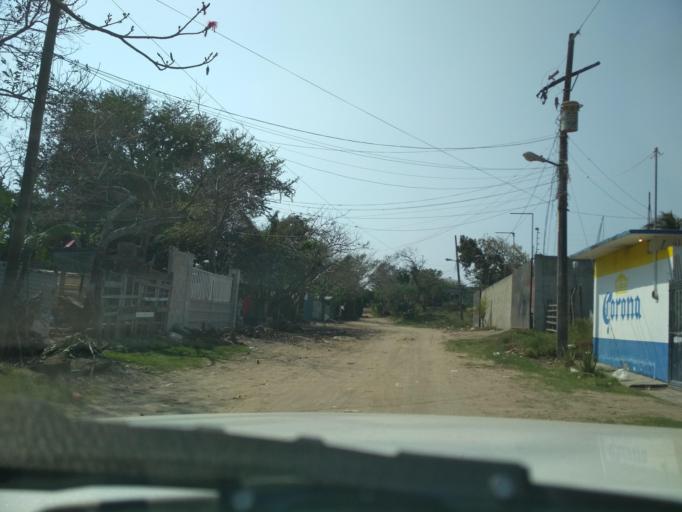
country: MX
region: Veracruz
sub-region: Veracruz
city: Rio Medio [Granja]
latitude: 19.2127
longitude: -96.2107
